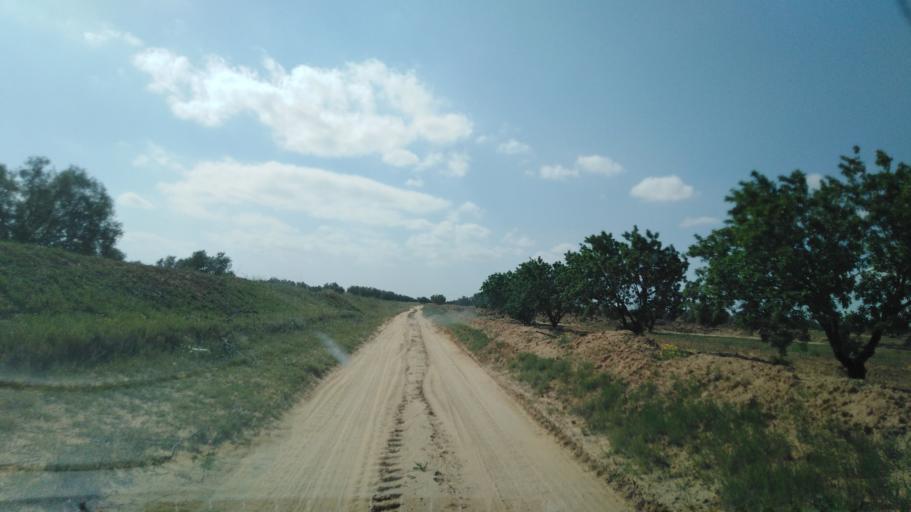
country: TN
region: Safaqis
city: Bi'r `Ali Bin Khalifah
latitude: 34.7913
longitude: 10.4025
